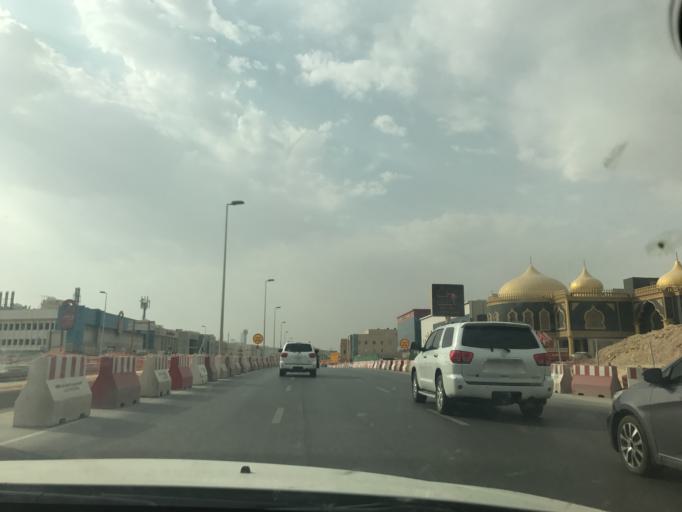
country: SA
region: Ar Riyad
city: Riyadh
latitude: 24.7145
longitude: 46.6979
